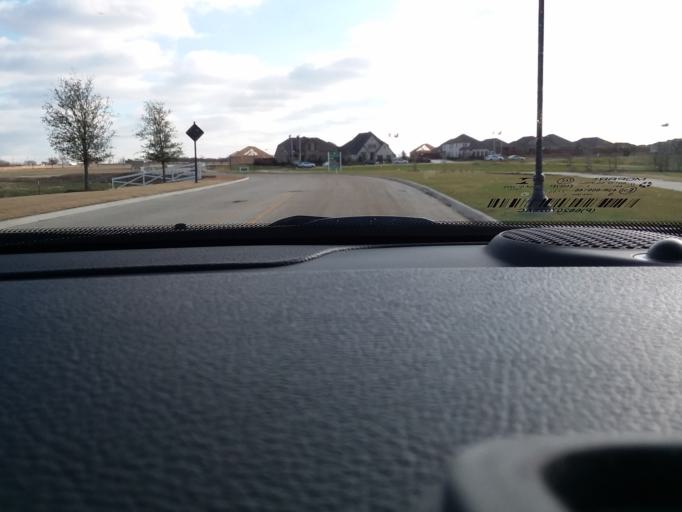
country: US
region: Texas
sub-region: Denton County
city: Krugerville
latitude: 33.2668
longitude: -96.8975
